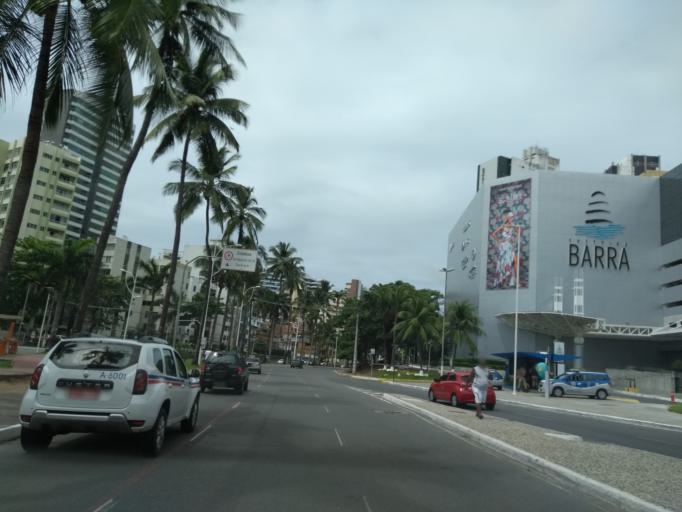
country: BR
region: Bahia
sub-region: Salvador
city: Salvador
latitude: -13.0058
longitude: -38.5234
